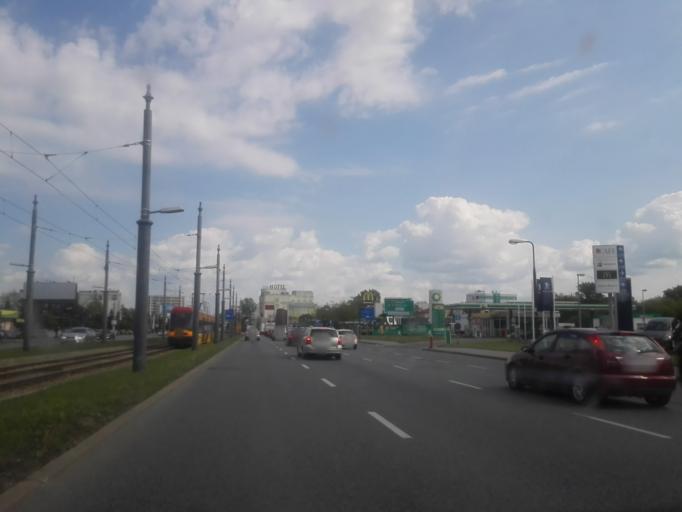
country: PL
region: Masovian Voivodeship
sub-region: Warszawa
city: Wlochy
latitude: 52.1843
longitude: 20.9528
